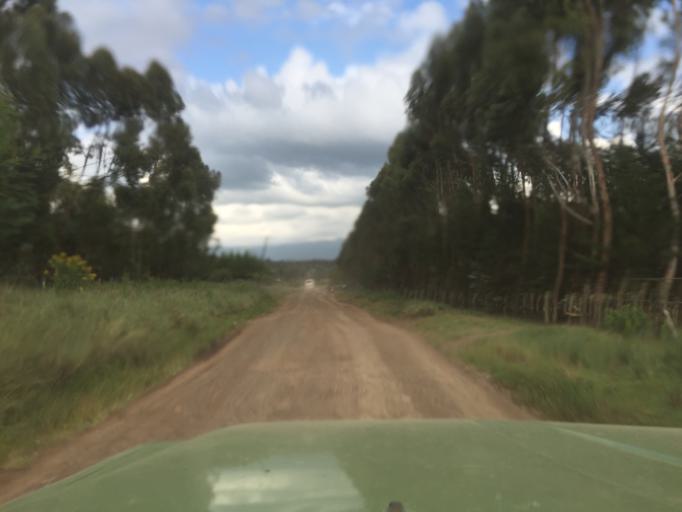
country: KE
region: Nyandarua
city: Ol Kalou
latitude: -0.4187
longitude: 36.4461
